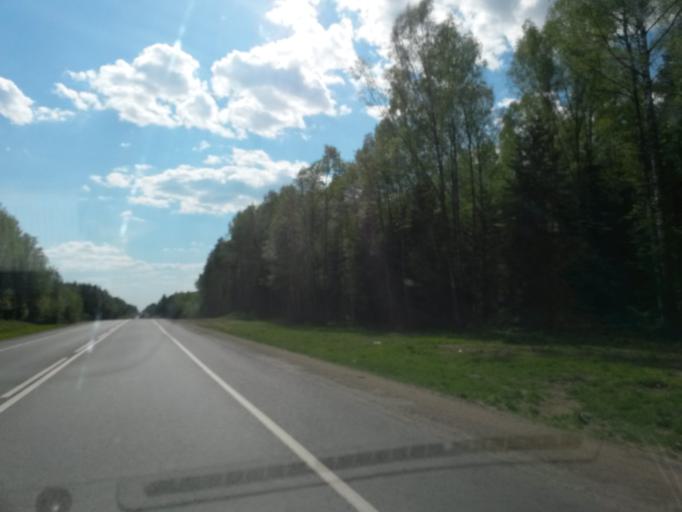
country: RU
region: Jaroslavl
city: Petrovsk
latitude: 56.9189
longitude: 39.1358
